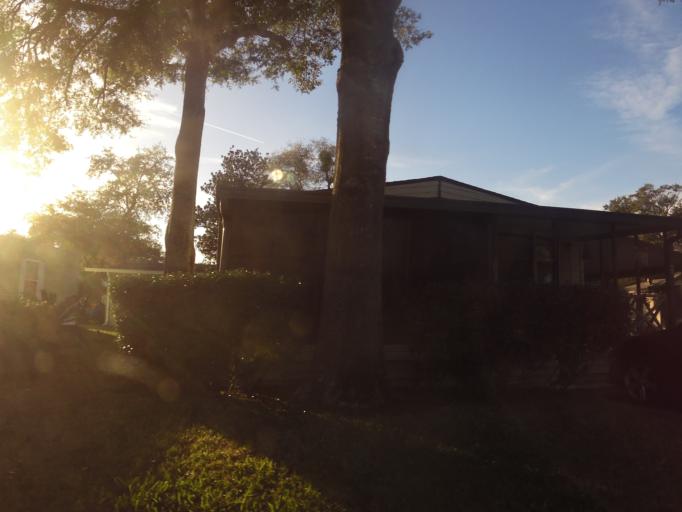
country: US
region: Florida
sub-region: Saint Johns County
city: Saint Augustine Shores
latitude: 29.8128
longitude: -81.3272
